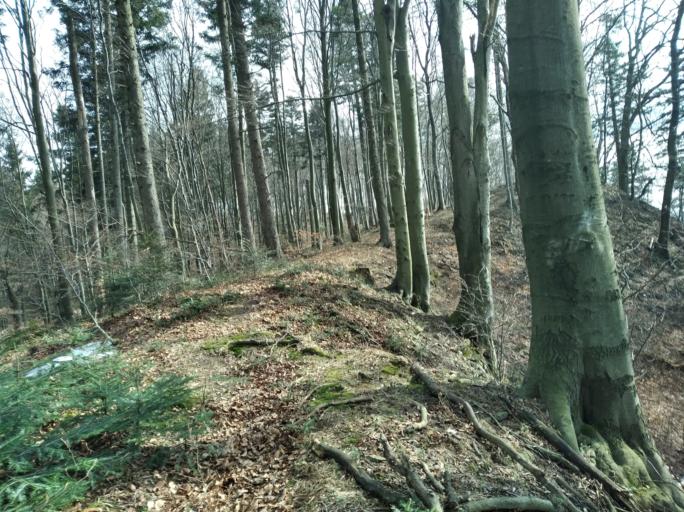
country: PL
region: Subcarpathian Voivodeship
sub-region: Powiat krosnienski
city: Korczyna
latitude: 49.7772
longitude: 21.8053
